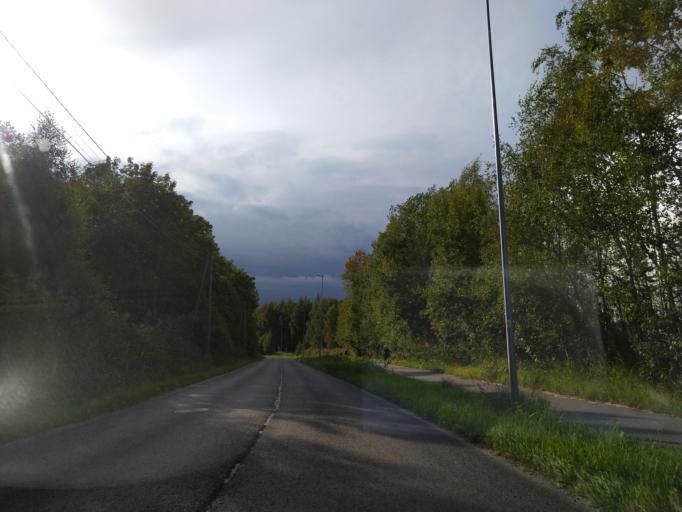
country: FI
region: Varsinais-Suomi
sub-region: Turku
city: Turku
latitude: 60.4293
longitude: 22.2230
